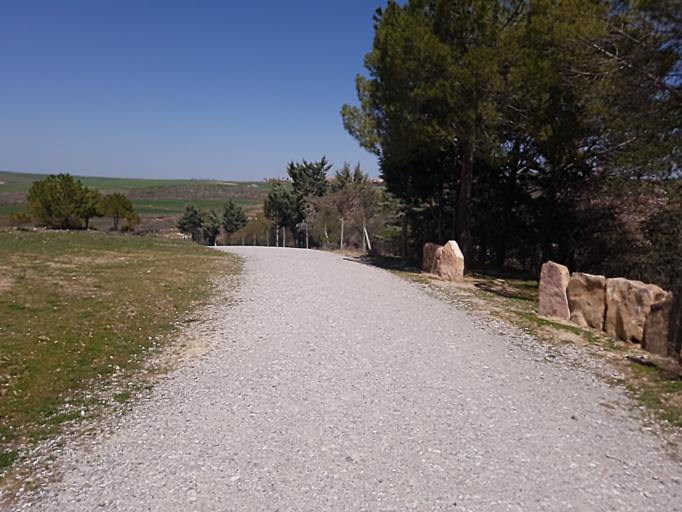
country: ES
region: Castille and Leon
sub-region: Provincia de Segovia
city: Segovia
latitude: 40.9513
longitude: -4.1345
